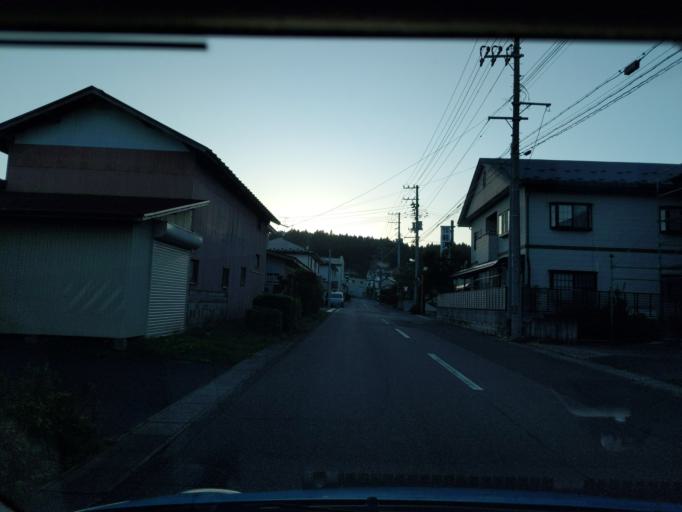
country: JP
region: Iwate
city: Mizusawa
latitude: 39.0468
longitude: 141.1252
